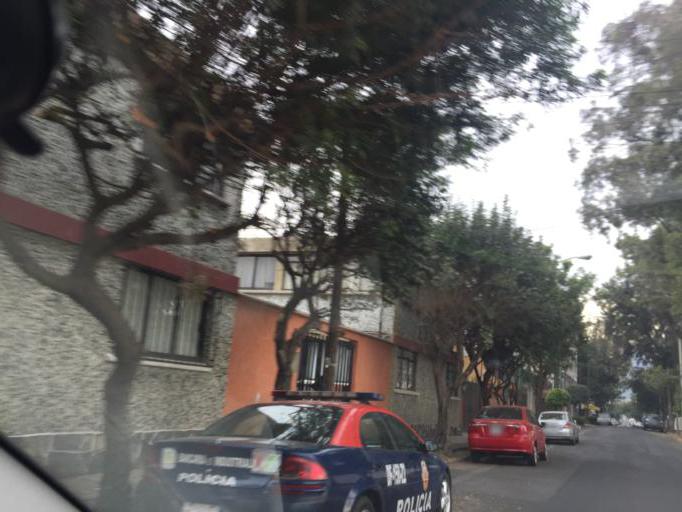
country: MX
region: Mexico
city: Colonia Lindavista
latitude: 19.4940
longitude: -99.1297
